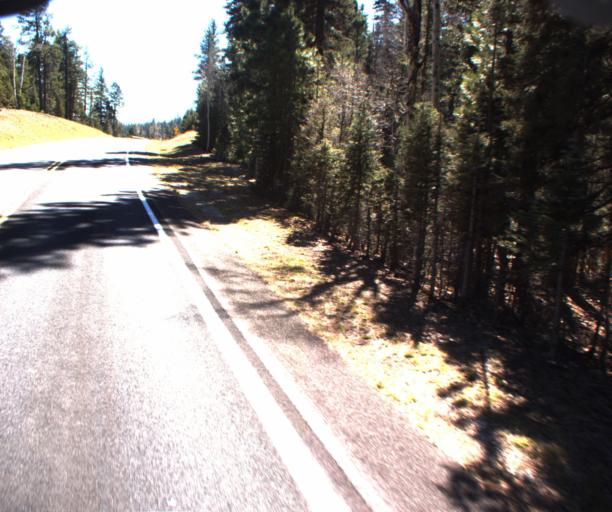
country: US
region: Arizona
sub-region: Coconino County
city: Grand Canyon
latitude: 36.5142
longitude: -112.1387
